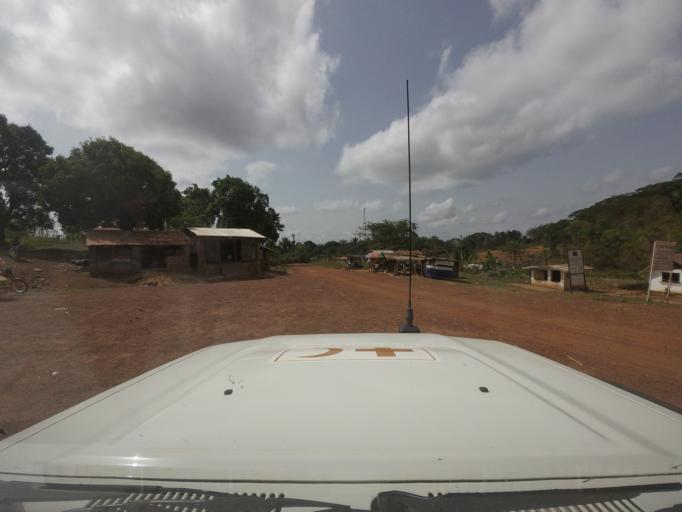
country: LR
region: Bong
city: Gbarnga
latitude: 7.2597
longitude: -9.4344
